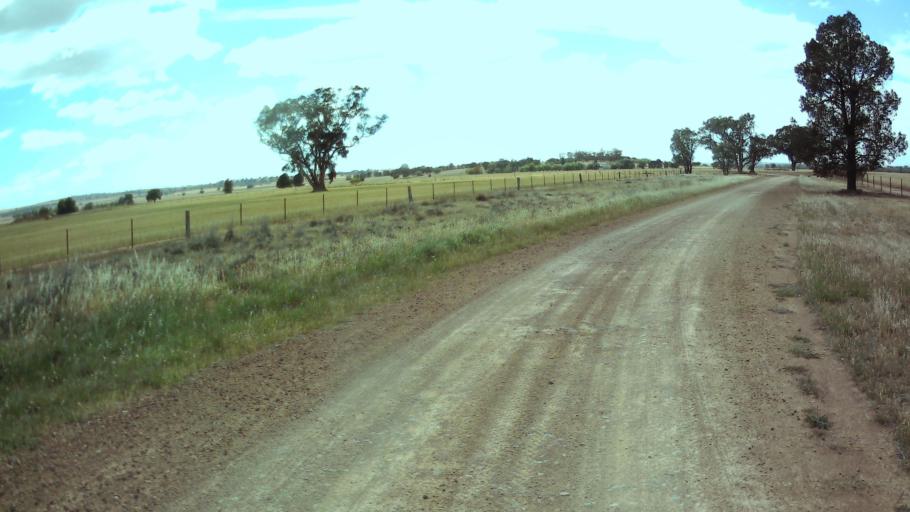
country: AU
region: New South Wales
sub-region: Weddin
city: Grenfell
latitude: -33.9978
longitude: 148.2996
